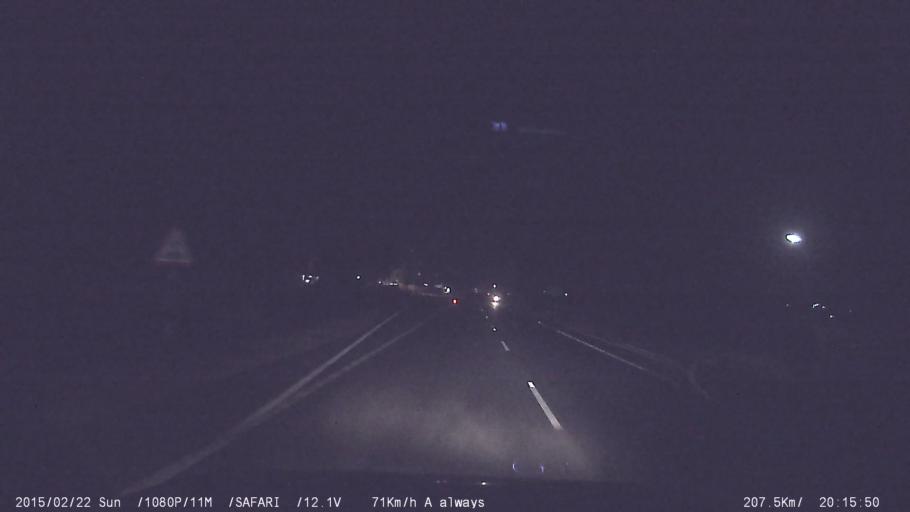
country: IN
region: Tamil Nadu
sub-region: Dindigul
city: Nilakottai
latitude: 10.2624
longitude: 77.8446
